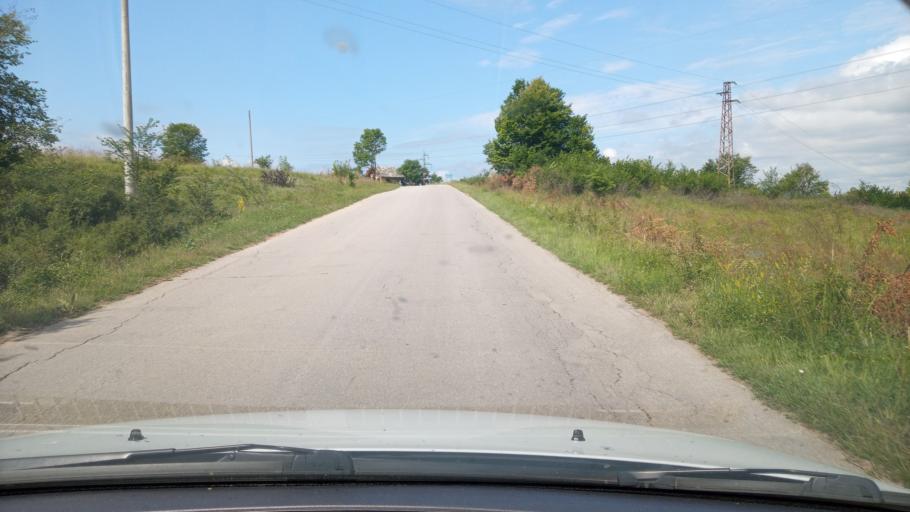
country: BG
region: Pleven
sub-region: Obshtina Cherven Bryag
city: Cherven Bryag
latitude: 43.1784
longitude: 24.0774
